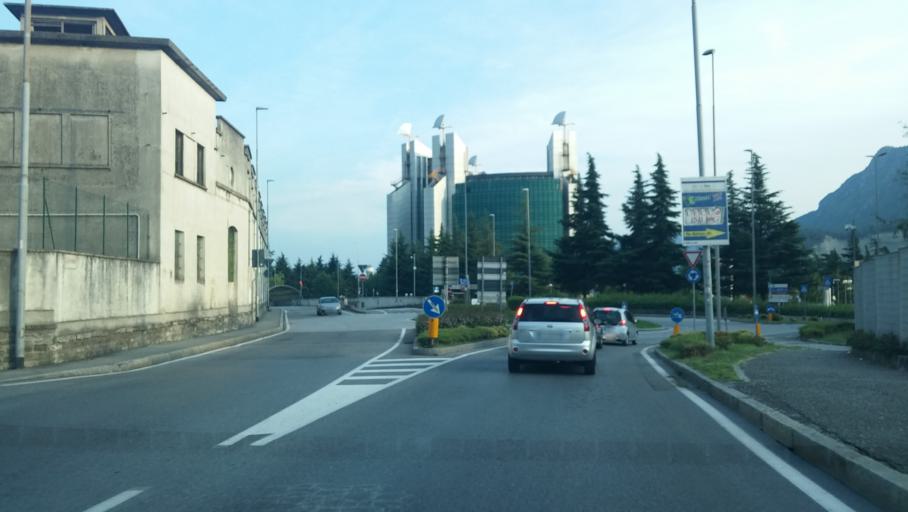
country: IT
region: Lombardy
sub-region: Provincia di Lecco
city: Lecco
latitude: 45.8566
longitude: 9.3978
